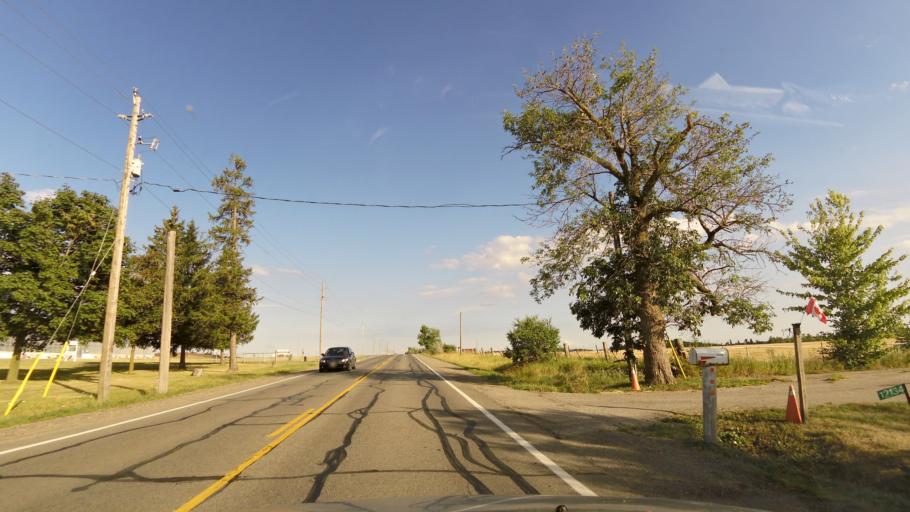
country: CA
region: Ontario
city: Brampton
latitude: 43.6974
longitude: -79.8710
